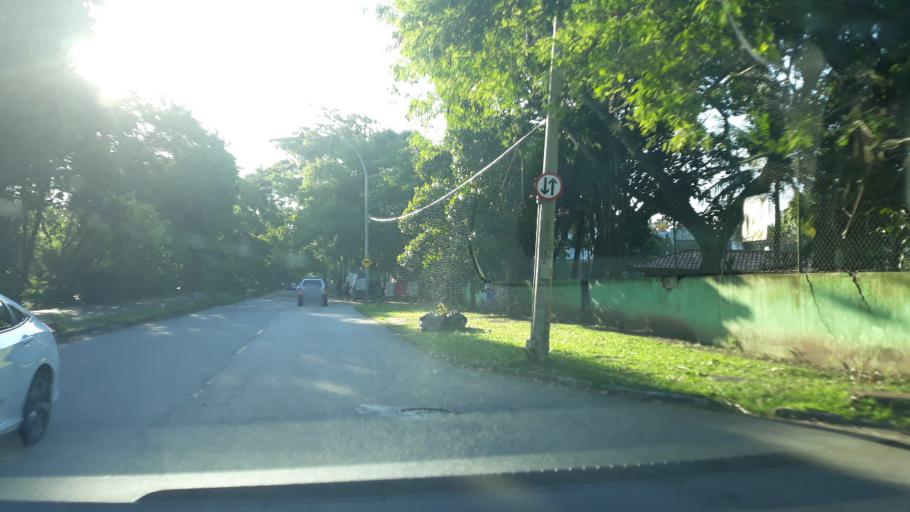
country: BR
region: Rio de Janeiro
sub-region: Rio De Janeiro
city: Rio de Janeiro
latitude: -23.0063
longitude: -43.3335
